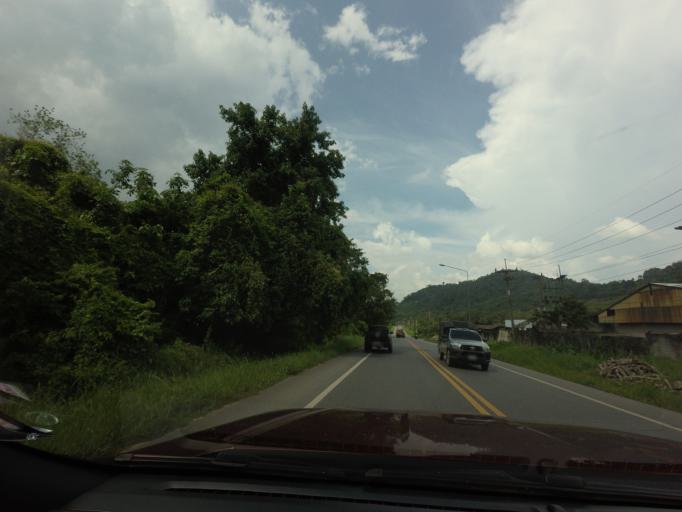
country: TH
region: Yala
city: Ban Nang Sata
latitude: 6.2526
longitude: 101.2260
